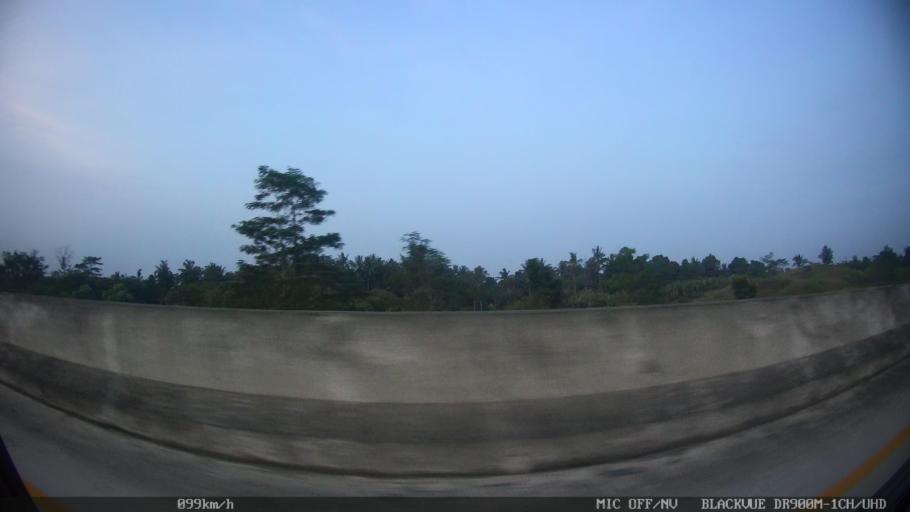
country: ID
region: Lampung
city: Kalianda
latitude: -5.6858
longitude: 105.6155
